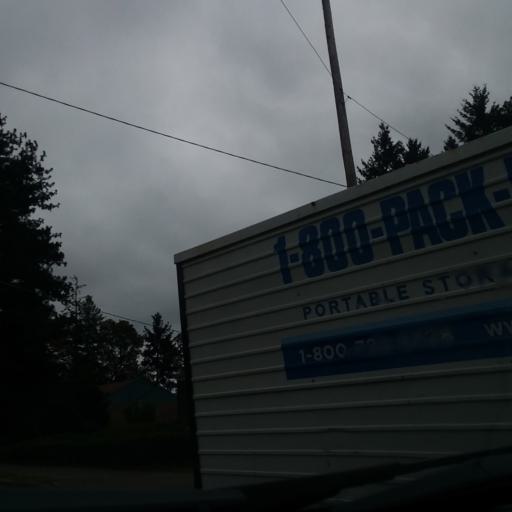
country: US
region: Washington
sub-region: King County
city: White Center
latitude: 47.5094
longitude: -122.3393
